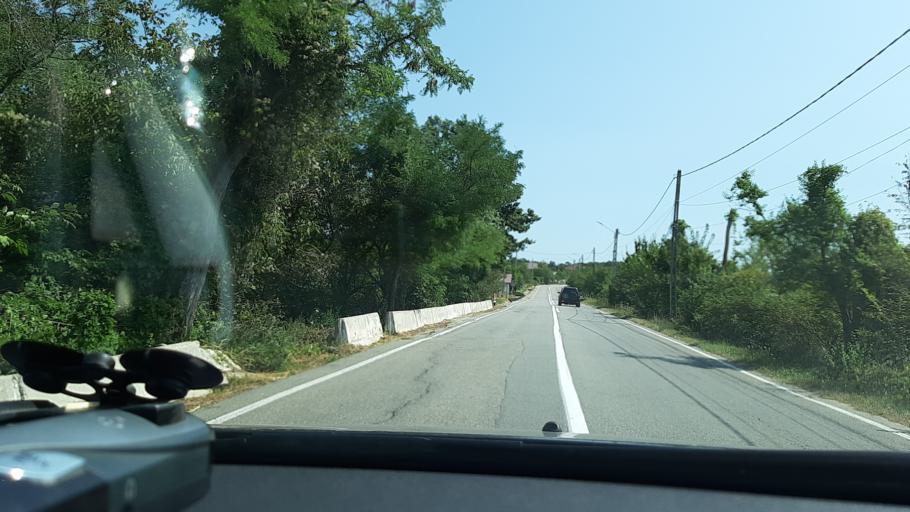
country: RO
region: Gorj
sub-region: Comuna Targu Carbunesti
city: Targu Carbunesti
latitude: 44.9511
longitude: 23.5463
